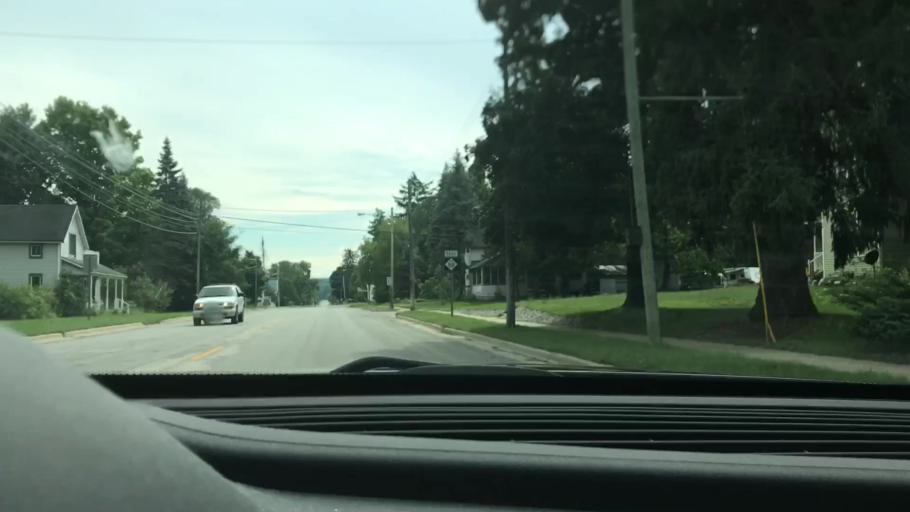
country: US
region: Michigan
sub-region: Antrim County
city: Bellaire
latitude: 45.0678
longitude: -85.2642
